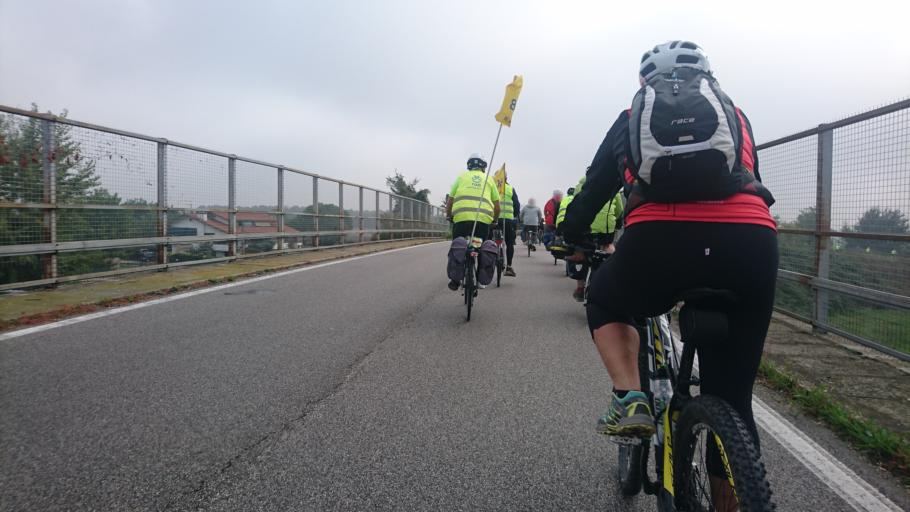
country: IT
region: Veneto
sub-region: Provincia di Padova
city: Pozzonovo
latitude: 45.2142
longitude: 11.7744
